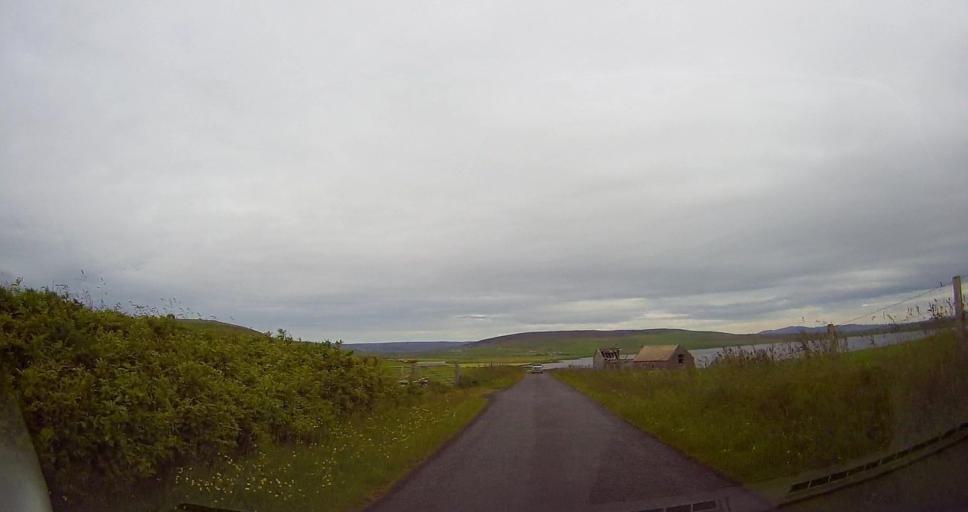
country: GB
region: Scotland
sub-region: Orkney Islands
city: Stromness
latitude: 59.1211
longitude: -3.2762
